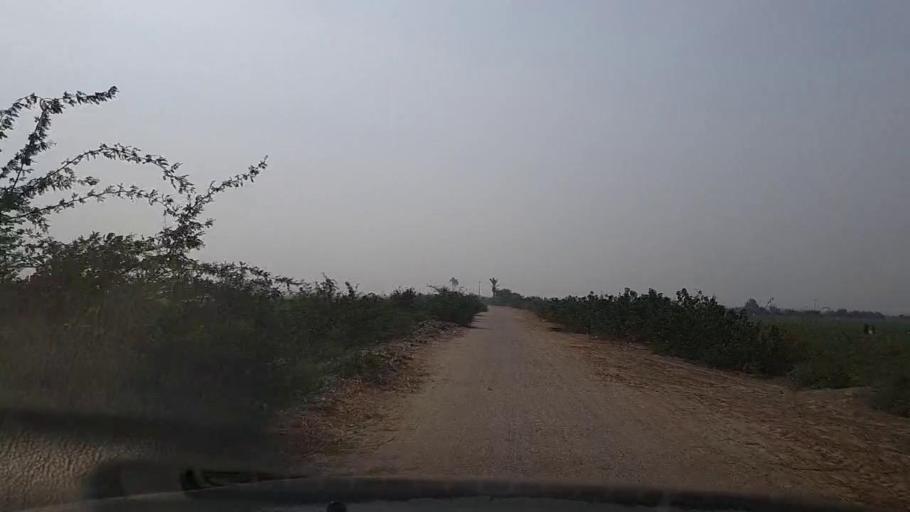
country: PK
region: Sindh
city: Mirpur Sakro
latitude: 24.5492
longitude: 67.8351
